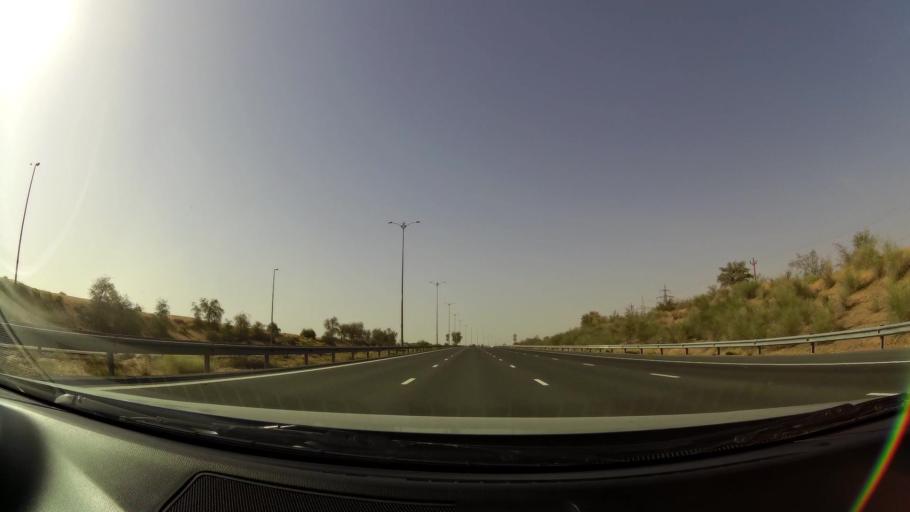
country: OM
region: Al Buraimi
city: Al Buraymi
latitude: 24.4574
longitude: 55.7819
